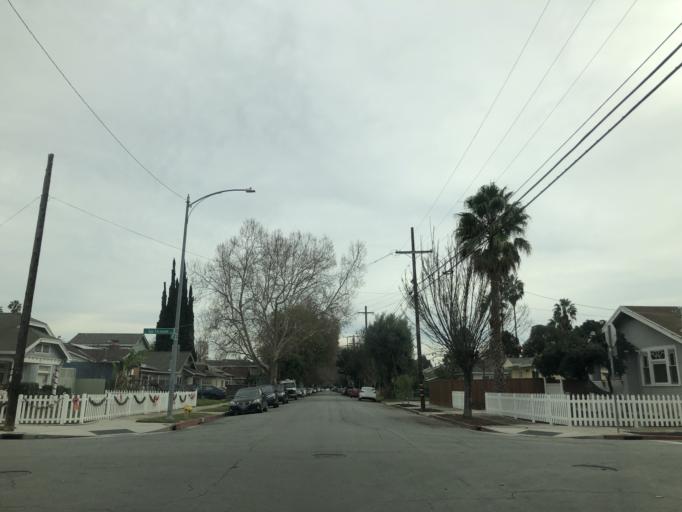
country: US
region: California
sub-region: Santa Clara County
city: San Jose
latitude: 37.3435
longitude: -121.8702
